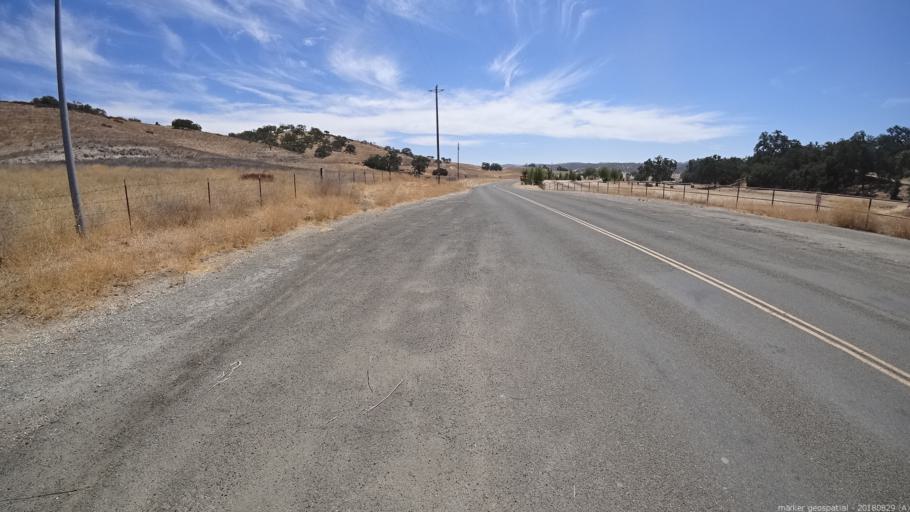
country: US
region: California
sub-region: San Luis Obispo County
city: Lake Nacimiento
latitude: 35.8811
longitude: -120.9909
